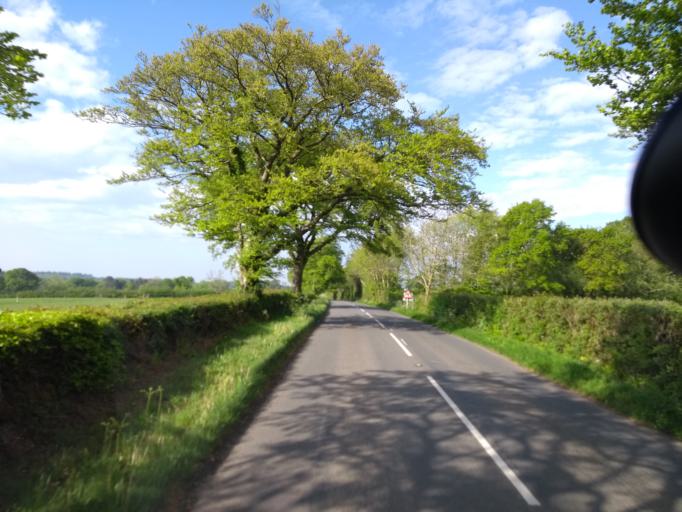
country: GB
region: England
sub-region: Dorset
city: Lyme Regis
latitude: 50.7773
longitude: -2.9413
